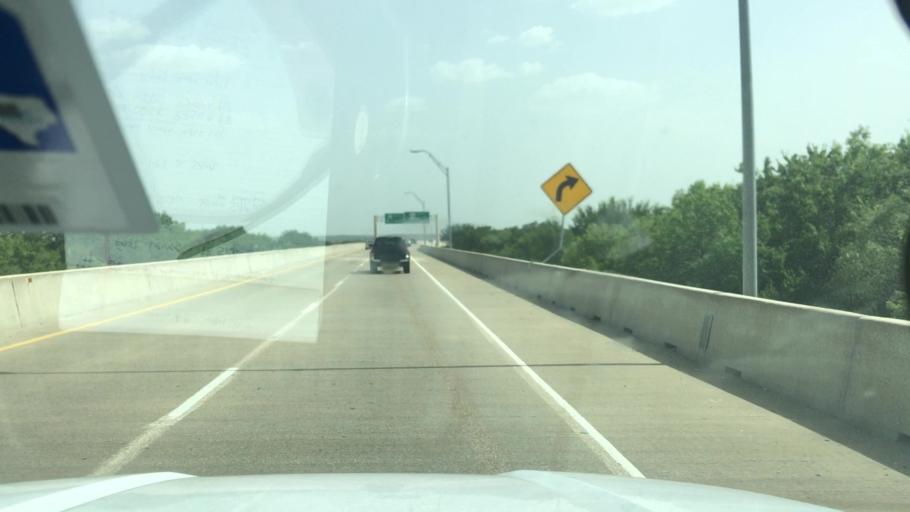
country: US
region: Texas
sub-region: Tarrant County
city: Grapevine
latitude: 32.9237
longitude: -97.0927
